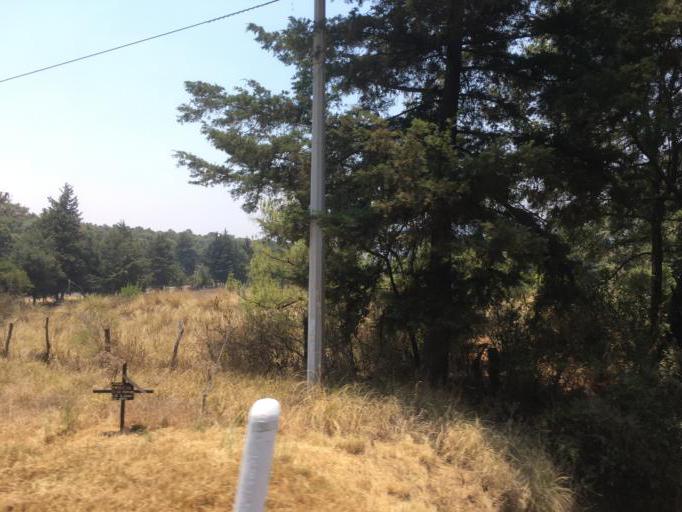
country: MX
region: Michoacan
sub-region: Morelia
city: Iratzio
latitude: 19.6214
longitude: -101.4611
